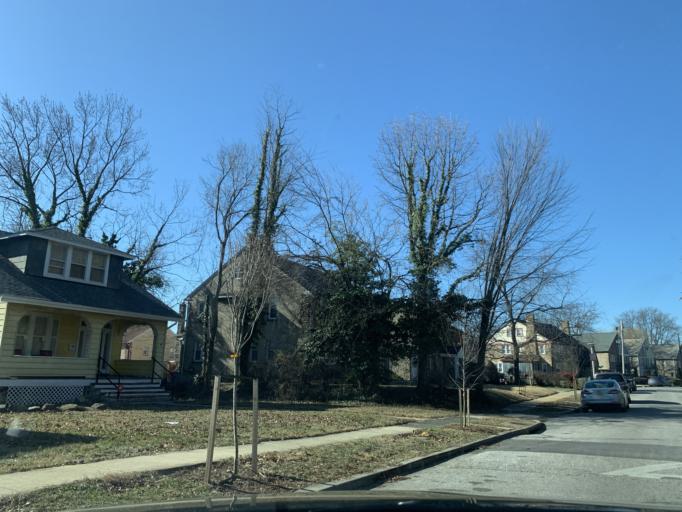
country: US
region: Maryland
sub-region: Baltimore County
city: Lochearn
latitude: 39.3305
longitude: -76.6877
